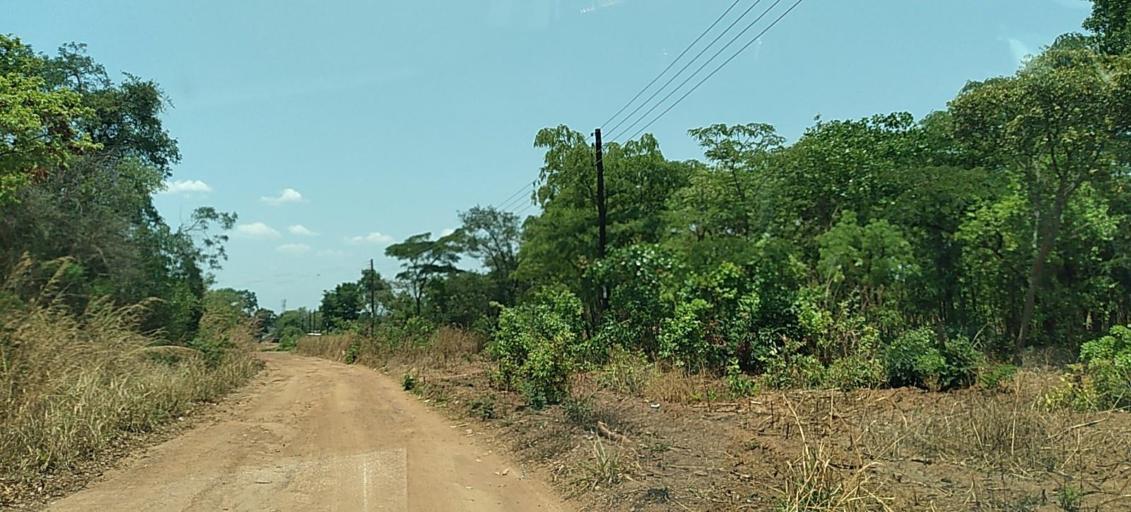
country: ZM
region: Copperbelt
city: Luanshya
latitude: -13.1066
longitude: 28.4047
